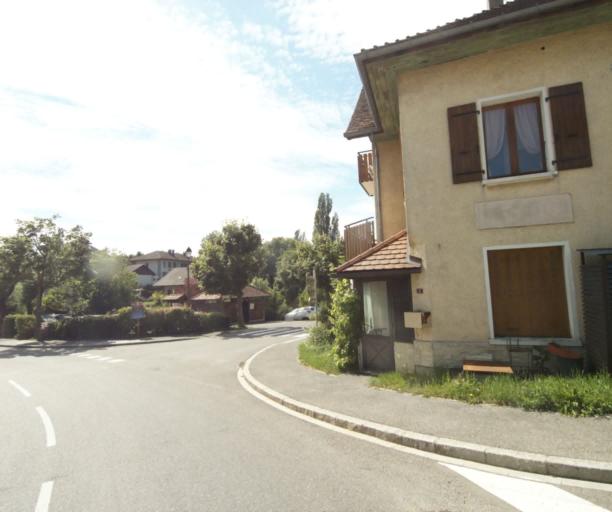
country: FR
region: Rhone-Alpes
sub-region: Departement de la Haute-Savoie
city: Perrignier
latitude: 46.3046
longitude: 6.4423
